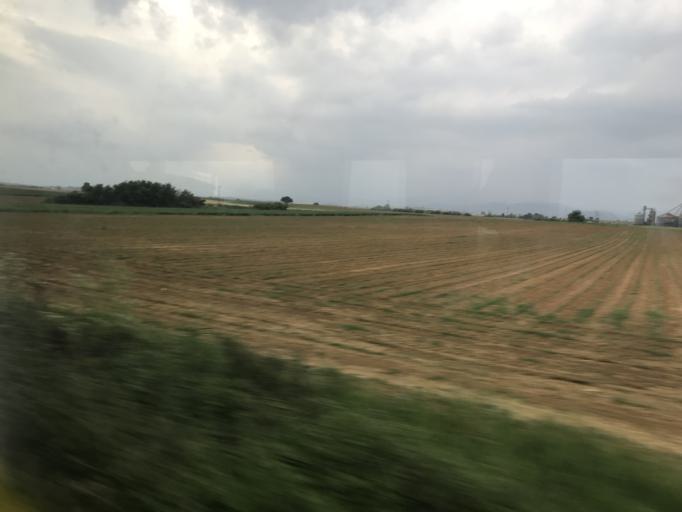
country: GR
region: East Macedonia and Thrace
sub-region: Nomos Rodopis
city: Aratos
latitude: 41.0851
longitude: 25.5312
